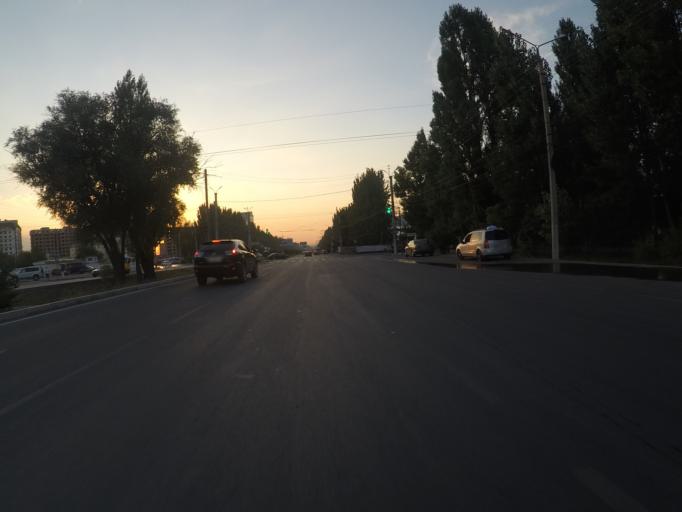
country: KG
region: Chuy
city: Bishkek
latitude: 42.8132
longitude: 74.6314
